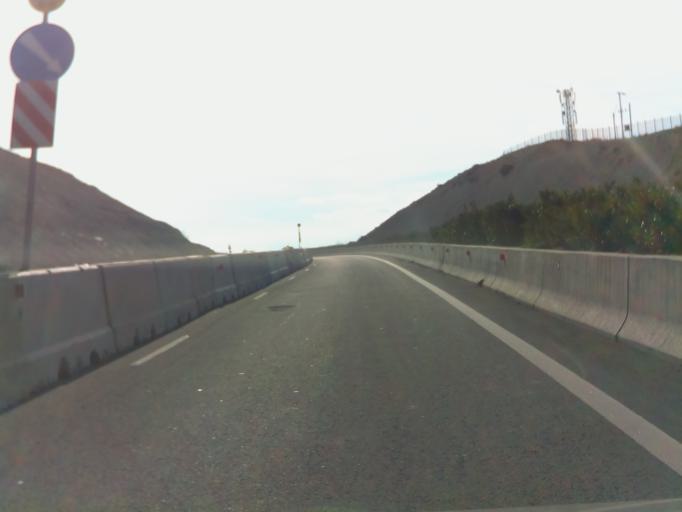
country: CY
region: Limassol
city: Pissouri
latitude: 34.6698
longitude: 32.6393
